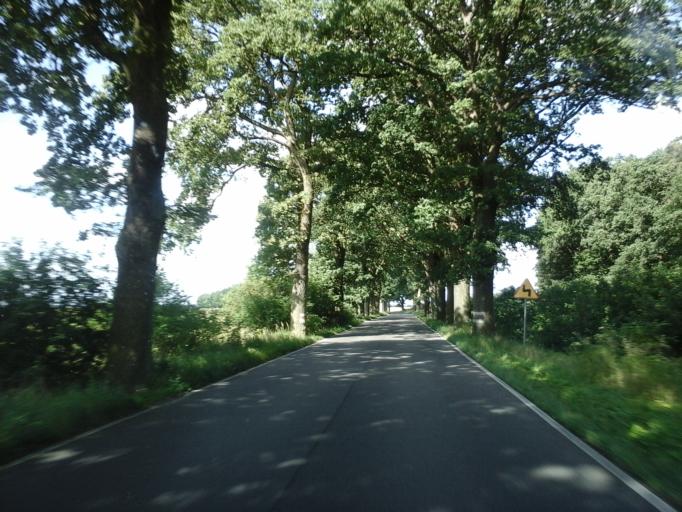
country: PL
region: West Pomeranian Voivodeship
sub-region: Powiat stargardzki
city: Dolice
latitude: 53.1984
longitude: 15.2459
